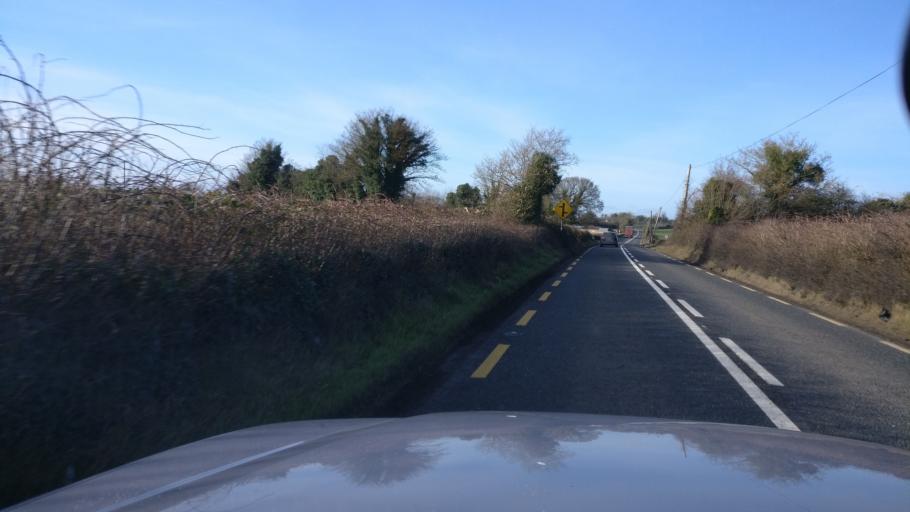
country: IE
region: Leinster
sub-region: Uibh Fhaili
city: Tullamore
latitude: 53.1934
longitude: -7.4126
